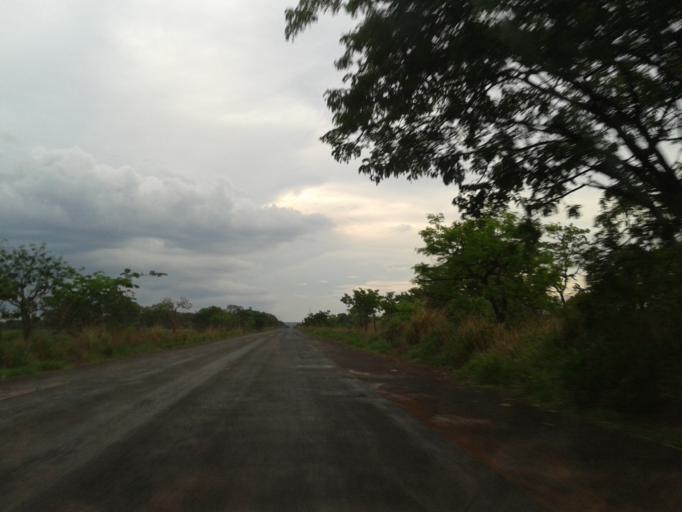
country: BR
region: Goias
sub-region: Quirinopolis
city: Quirinopolis
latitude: -18.1640
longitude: -50.4598
